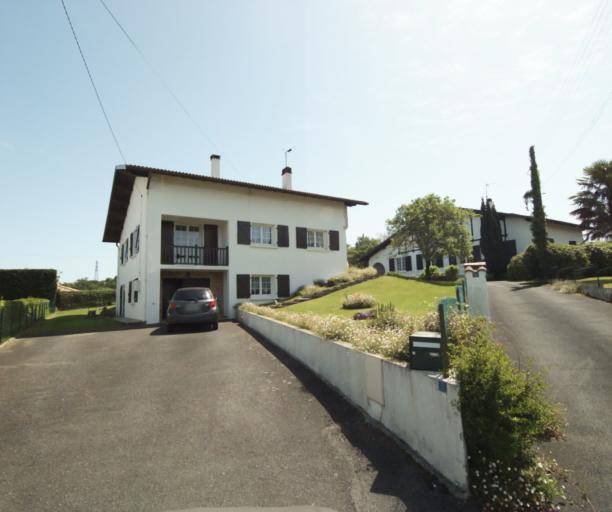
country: FR
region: Aquitaine
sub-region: Departement des Pyrenees-Atlantiques
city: Mouguerre
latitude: 43.4683
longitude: -1.4445
